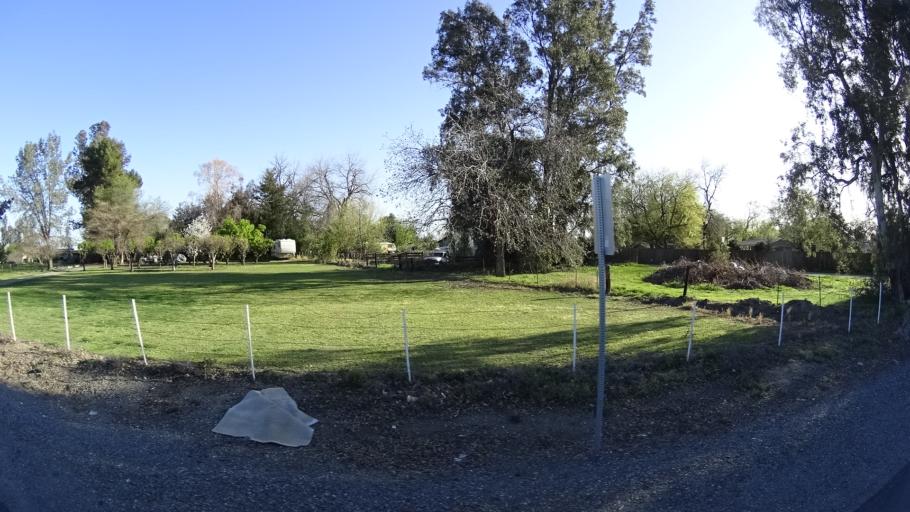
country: US
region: California
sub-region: Glenn County
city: Orland
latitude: 39.7533
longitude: -122.2119
